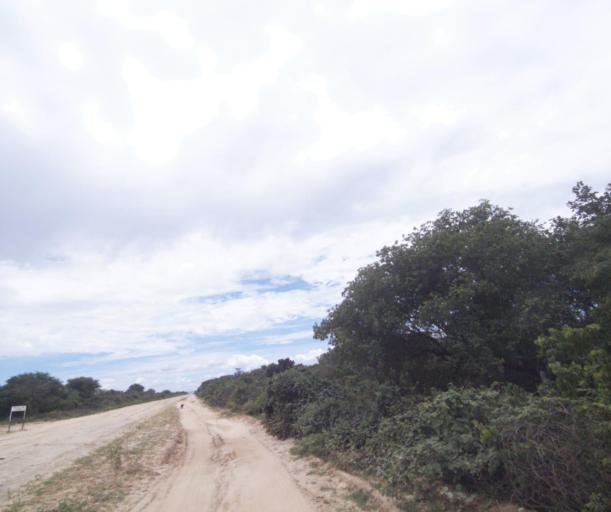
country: BR
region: Bahia
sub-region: Carinhanha
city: Carinhanha
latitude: -14.2587
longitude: -43.8250
